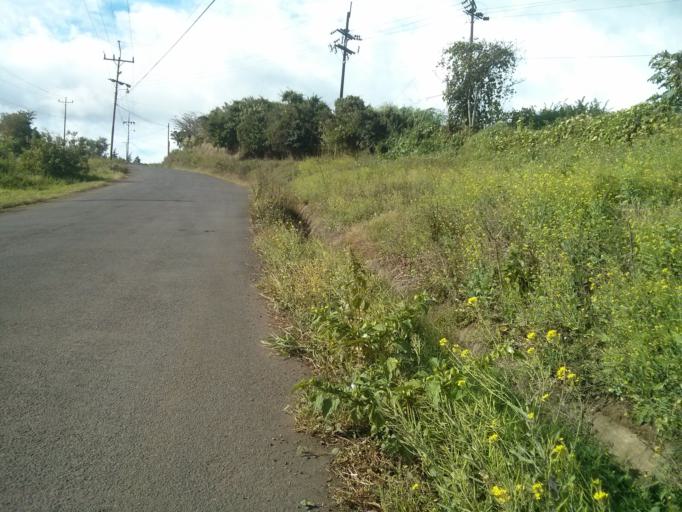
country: CR
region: Cartago
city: Cartago
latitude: 9.9030
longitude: -83.9423
